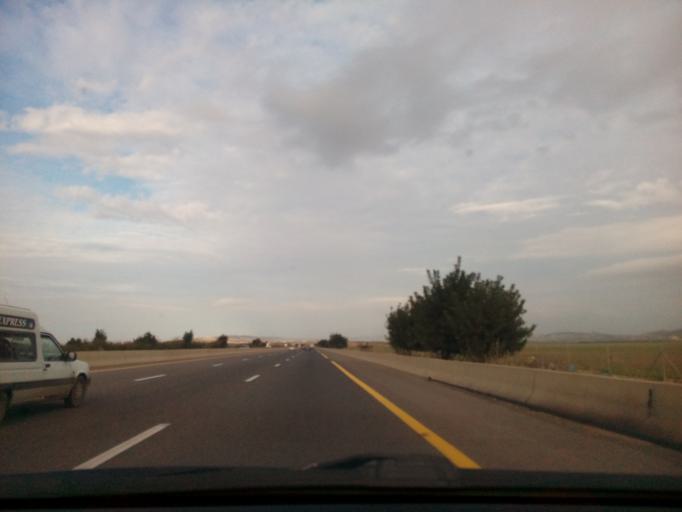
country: DZ
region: Mostaganem
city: Mostaganem
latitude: 35.6732
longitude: 0.1470
